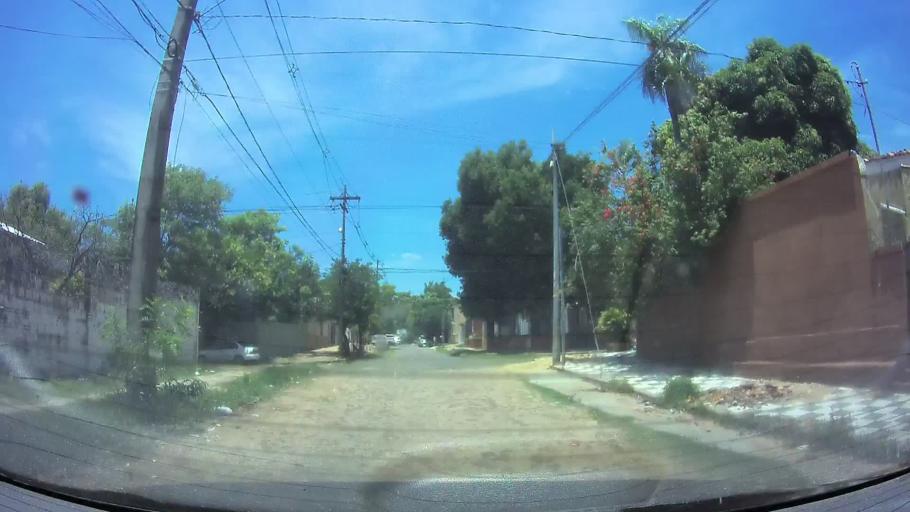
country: PY
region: Asuncion
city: Asuncion
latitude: -25.2720
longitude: -57.6008
